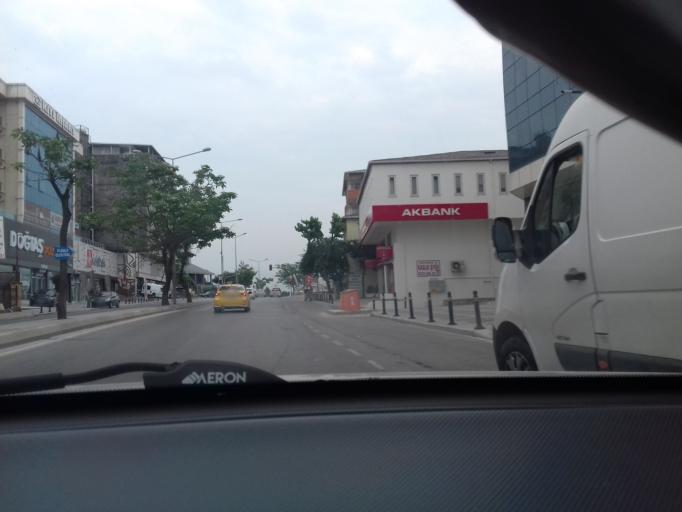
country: TR
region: Istanbul
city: Pendik
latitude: 40.9076
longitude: 29.2919
